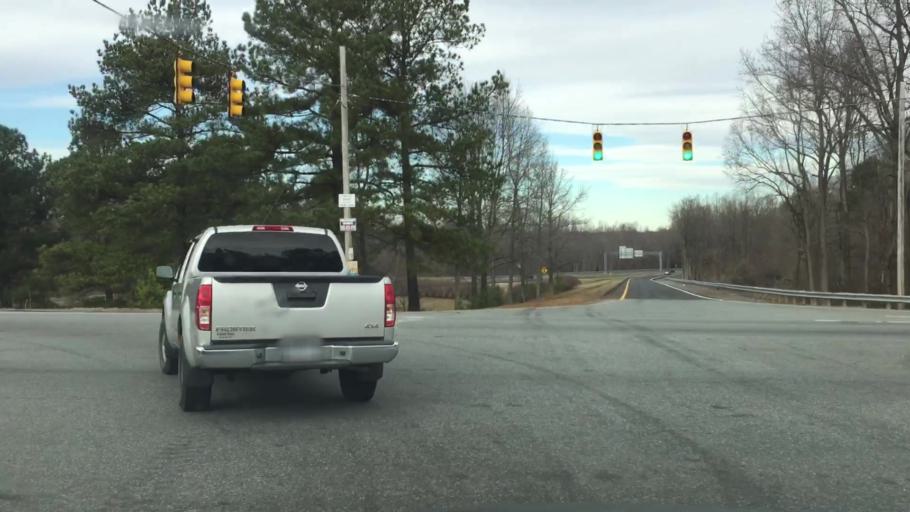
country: US
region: North Carolina
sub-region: Rockingham County
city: Reidsville
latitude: 36.3600
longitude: -79.6263
